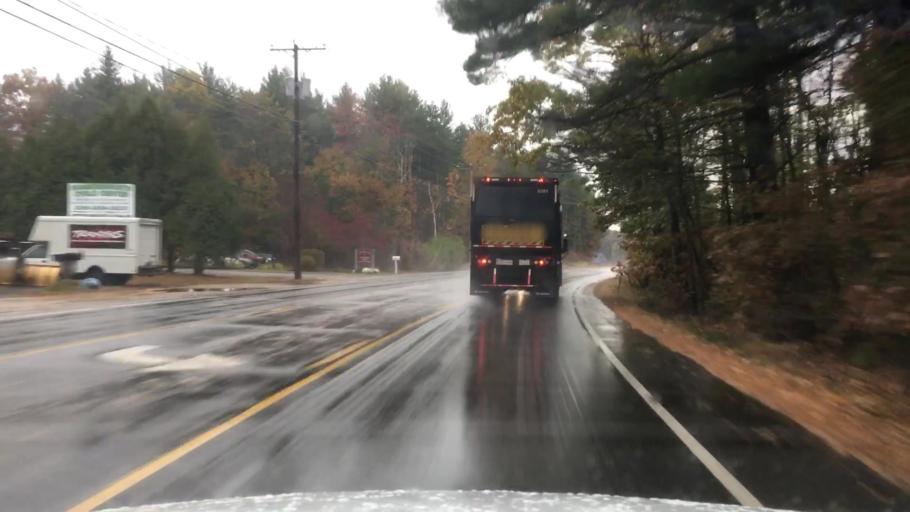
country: US
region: New Hampshire
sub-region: Strafford County
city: Somersworth
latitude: 43.2505
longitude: -70.8998
